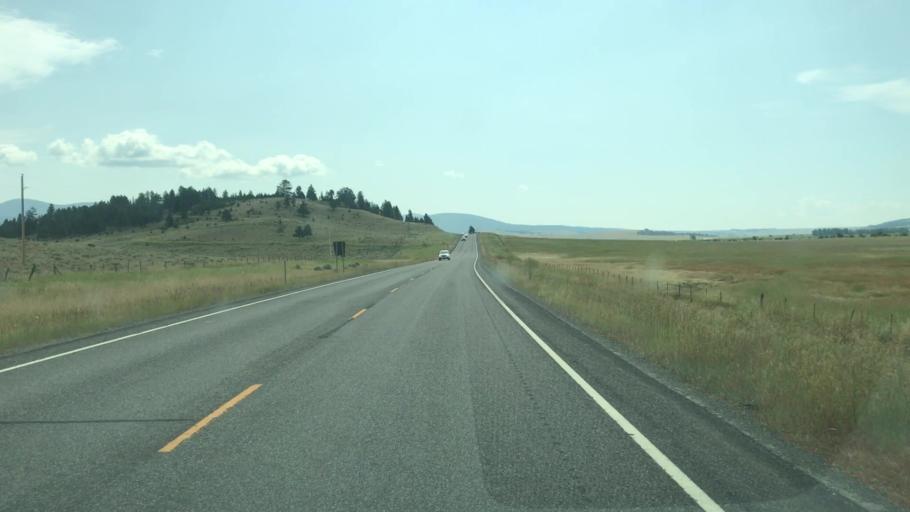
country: US
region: Montana
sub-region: Lewis and Clark County
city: Lincoln
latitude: 46.7730
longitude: -112.7351
